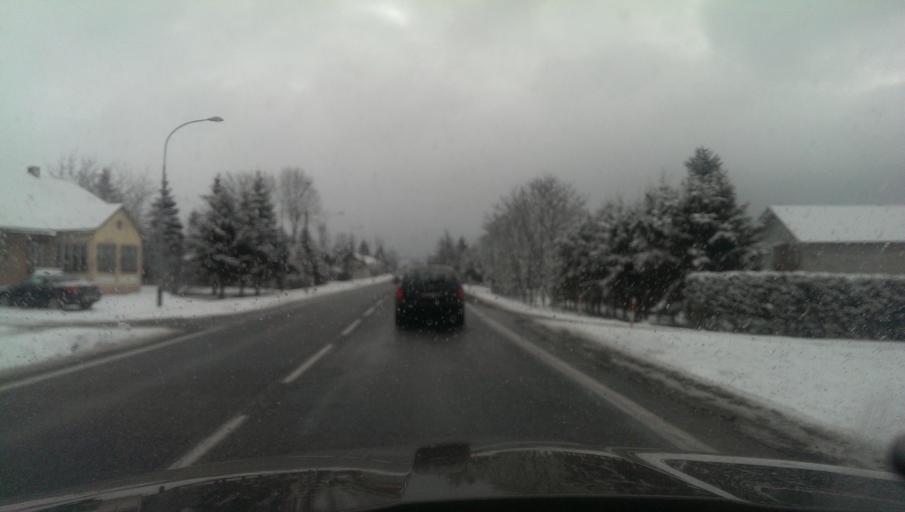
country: PL
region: Subcarpathian Voivodeship
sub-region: Powiat krosnienski
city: Miejsce Piastowe
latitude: 49.6131
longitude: 21.8009
